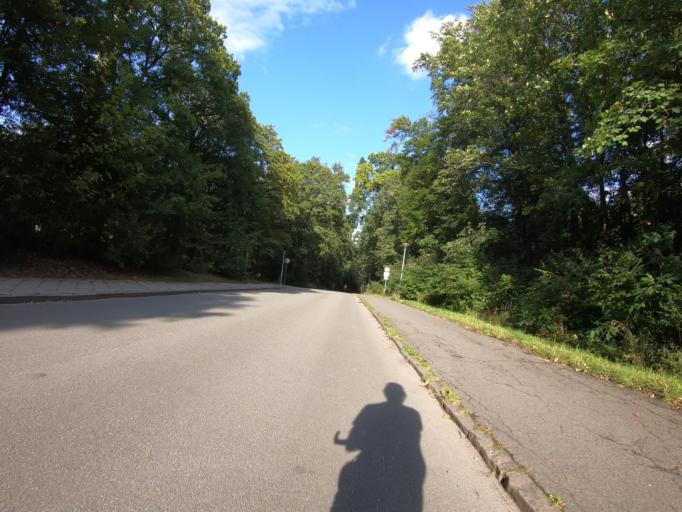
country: DE
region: Lower Saxony
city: Wolfsburg
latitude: 52.4137
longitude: 10.7742
